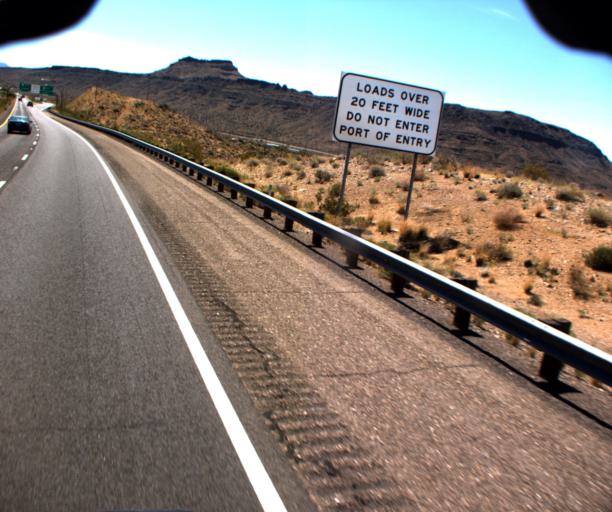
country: US
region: Arizona
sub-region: Mohave County
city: Golden Valley
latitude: 35.2275
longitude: -114.1343
